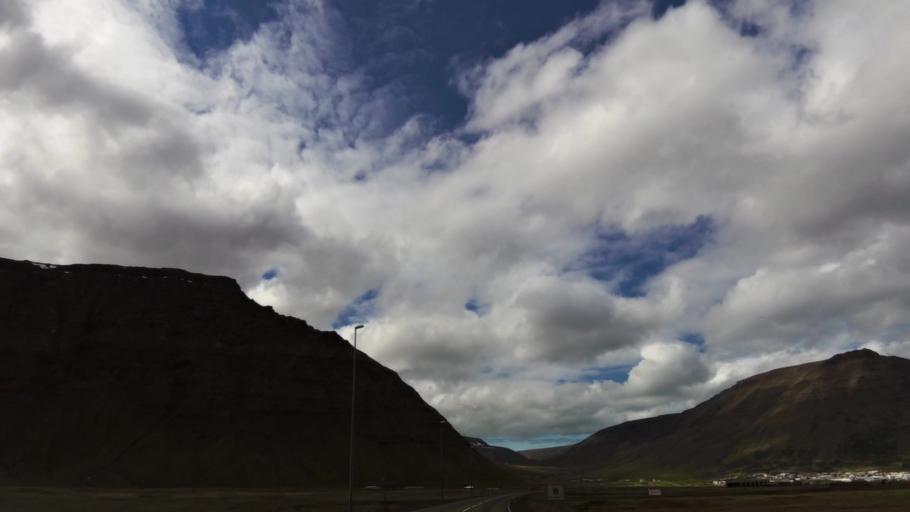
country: IS
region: Westfjords
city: Isafjoerdur
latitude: 66.1442
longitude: -23.2300
